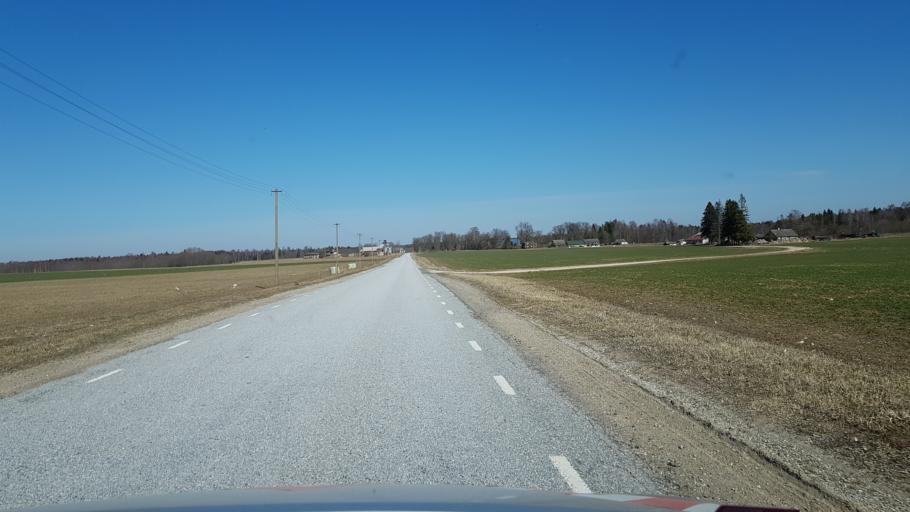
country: EE
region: Laeaene-Virumaa
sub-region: Tamsalu vald
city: Tamsalu
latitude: 59.0614
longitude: 26.1051
